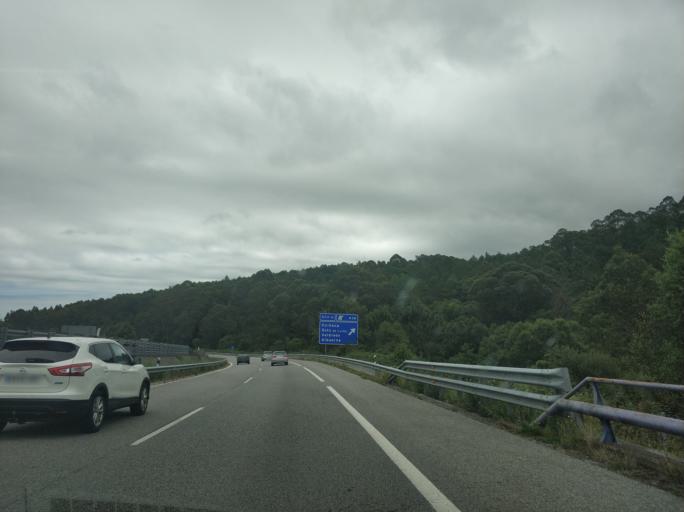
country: ES
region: Asturias
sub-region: Province of Asturias
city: Cudillero
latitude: 43.5620
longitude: -6.2531
